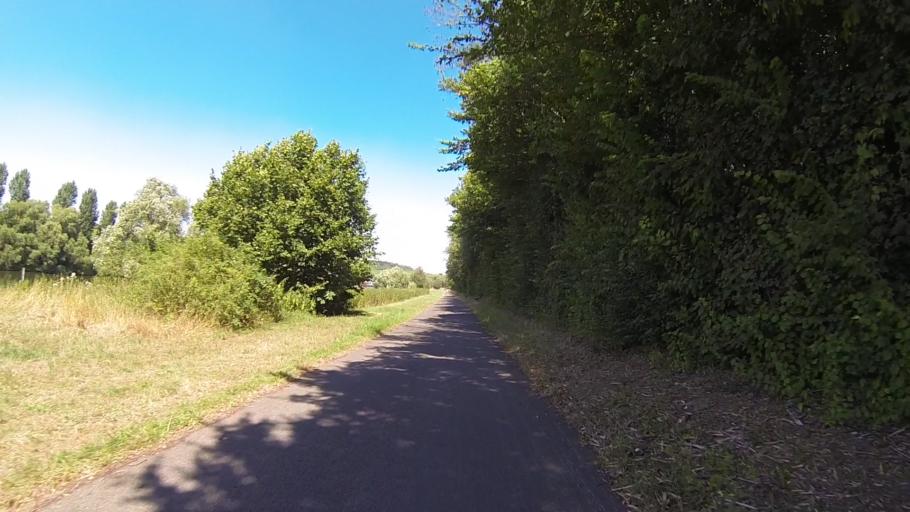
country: DE
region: Rheinland-Pfalz
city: Temmels
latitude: 49.6845
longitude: 6.4548
